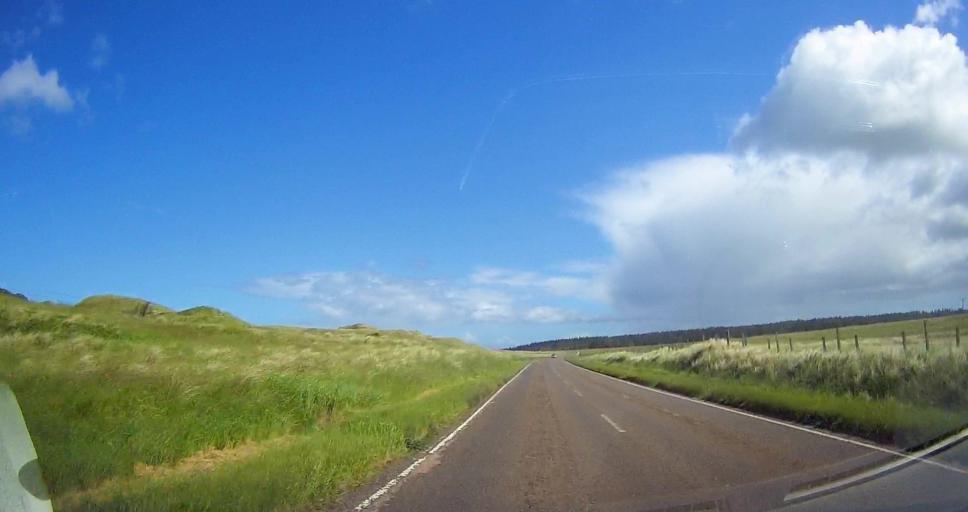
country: GB
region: Scotland
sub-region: Highland
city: Thurso
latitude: 58.6026
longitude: -3.3485
